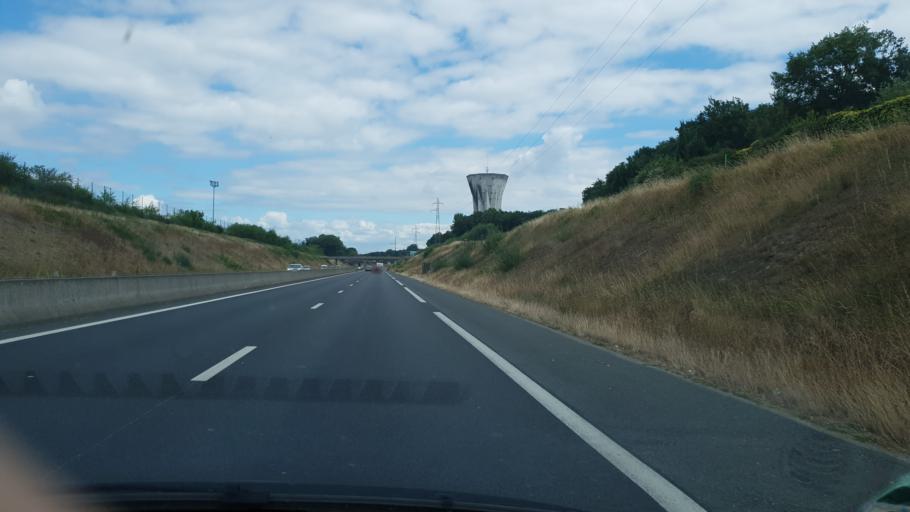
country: FR
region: Centre
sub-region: Departement d'Indre-et-Loire
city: Joue-les-Tours
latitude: 47.3408
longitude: 0.6553
